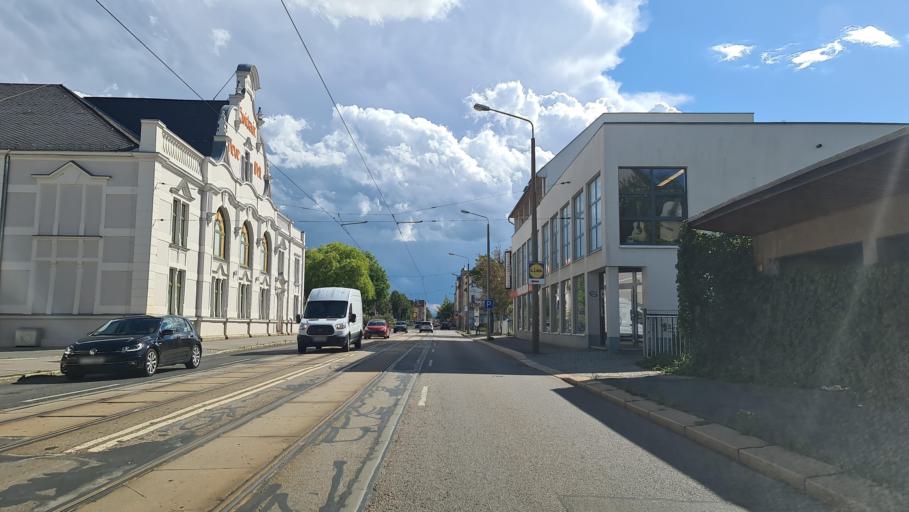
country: DE
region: Saxony
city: Zwickau
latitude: 50.7408
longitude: 12.4886
